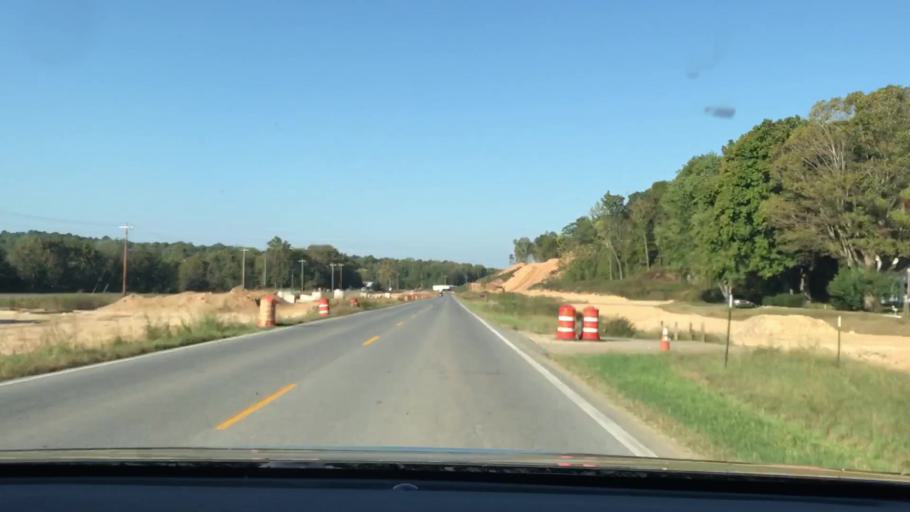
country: US
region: Kentucky
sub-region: Trigg County
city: Cadiz
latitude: 36.8056
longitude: -87.9126
